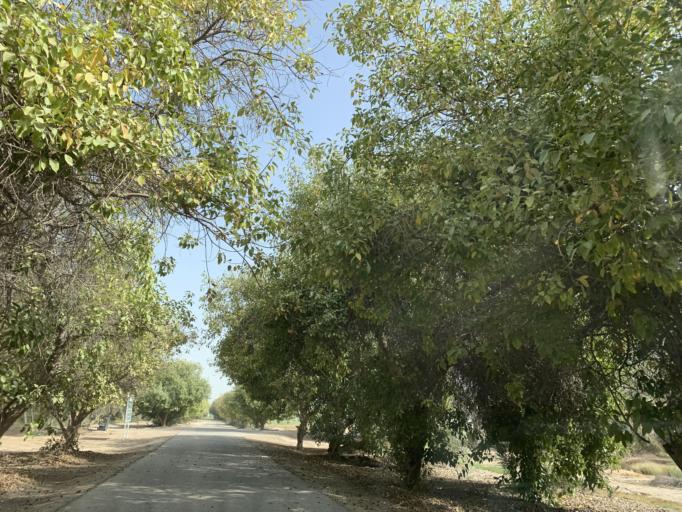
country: BH
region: Northern
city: Madinat `Isa
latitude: 26.1660
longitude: 50.5300
